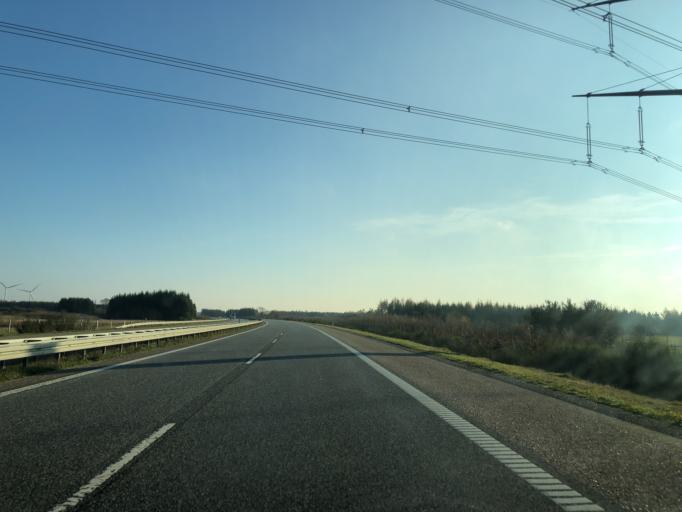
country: DK
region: Central Jutland
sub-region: Ikast-Brande Kommune
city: Brande
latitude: 55.9181
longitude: 9.1722
